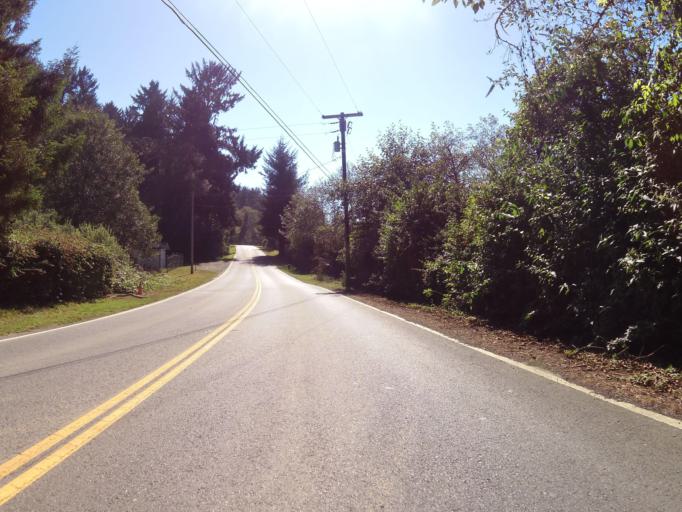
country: US
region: Oregon
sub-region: Curry County
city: Harbor
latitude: 41.9588
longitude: -124.2000
